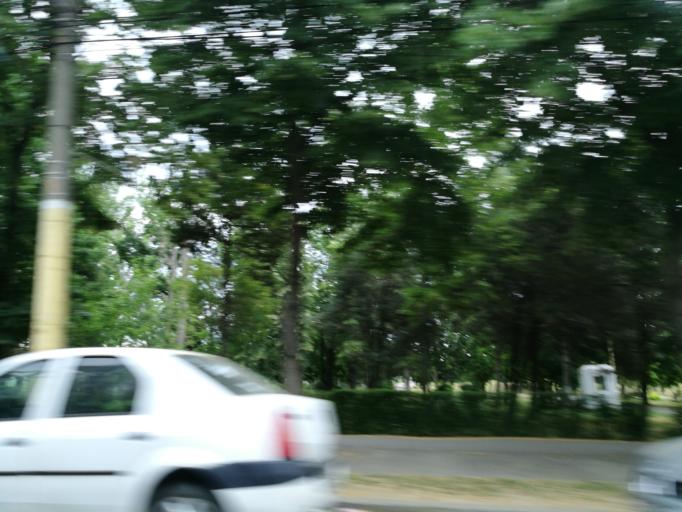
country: RO
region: Constanta
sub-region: Municipiul Constanta
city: Constanta
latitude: 44.2065
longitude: 28.6294
